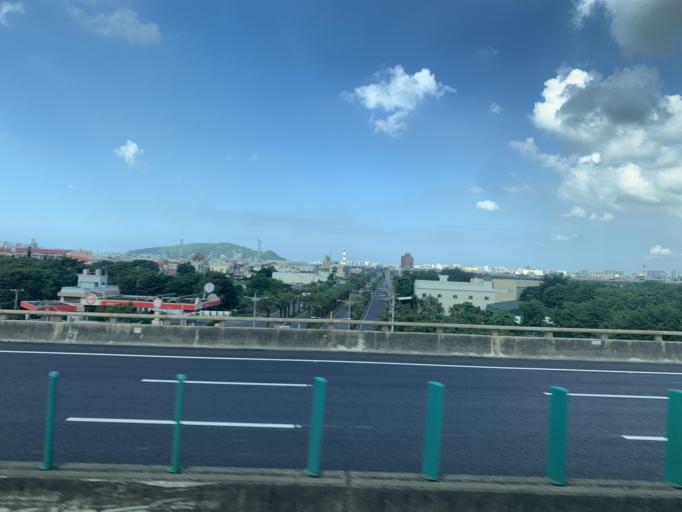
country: TW
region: Taiwan
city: Fengshan
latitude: 22.7038
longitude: 120.3600
